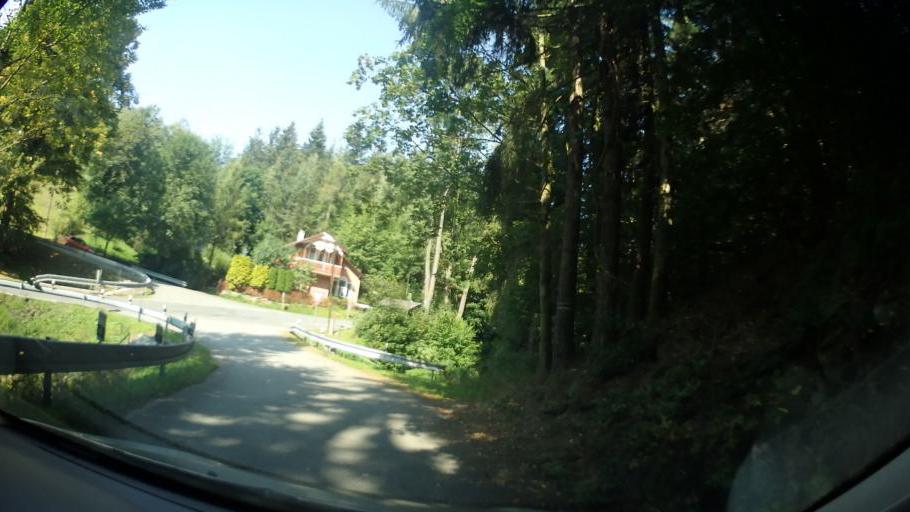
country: CZ
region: Pardubicky
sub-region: Okres Svitavy
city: Bystre
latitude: 49.5686
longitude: 16.3447
